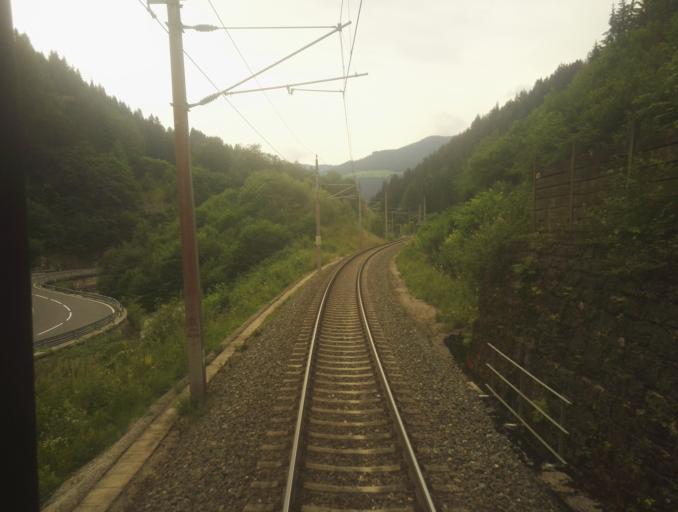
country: AT
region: Salzburg
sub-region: Politischer Bezirk Sankt Johann im Pongau
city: Huttau
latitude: 47.4232
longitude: 13.2934
